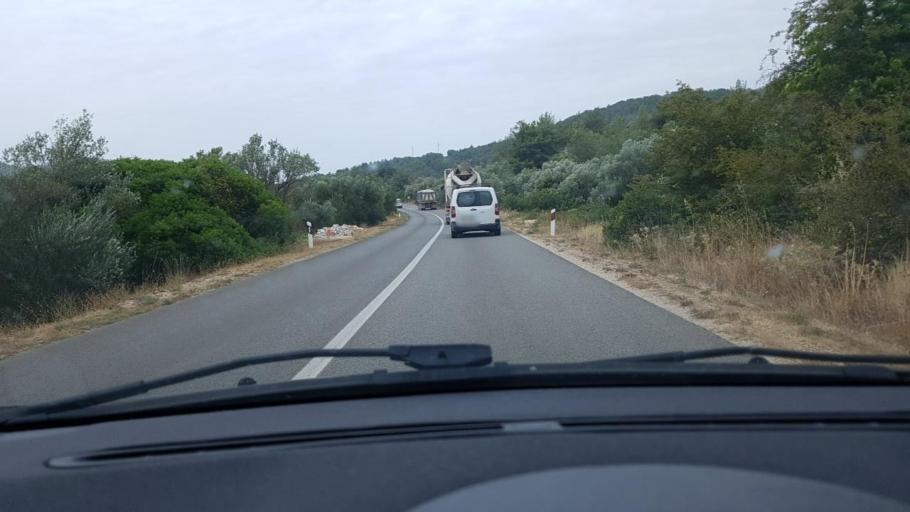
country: HR
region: Dubrovacko-Neretvanska
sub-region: Grad Dubrovnik
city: Vela Luka
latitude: 42.9495
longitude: 16.7600
